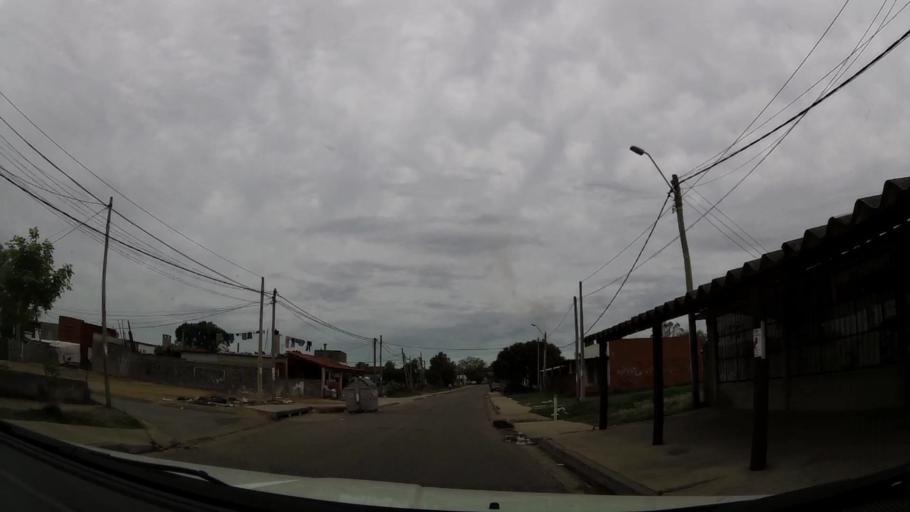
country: UY
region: Maldonado
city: Maldonado
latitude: -34.8963
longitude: -54.9358
